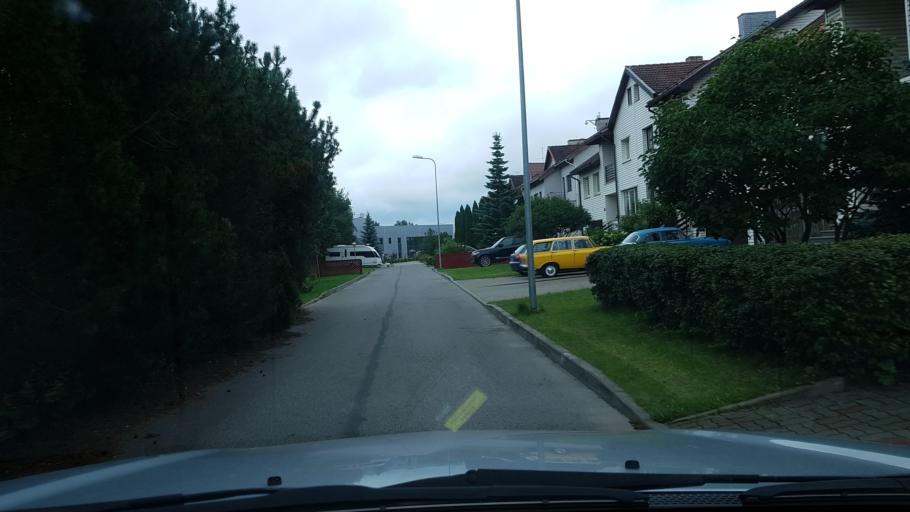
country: EE
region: Harju
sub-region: Tallinna linn
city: Tallinn
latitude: 59.4042
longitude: 24.8165
